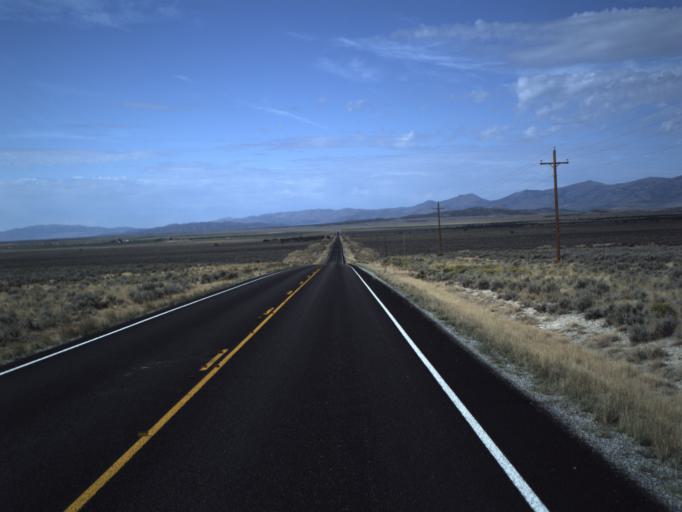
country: US
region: Idaho
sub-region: Cassia County
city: Burley
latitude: 41.7965
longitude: -113.4636
